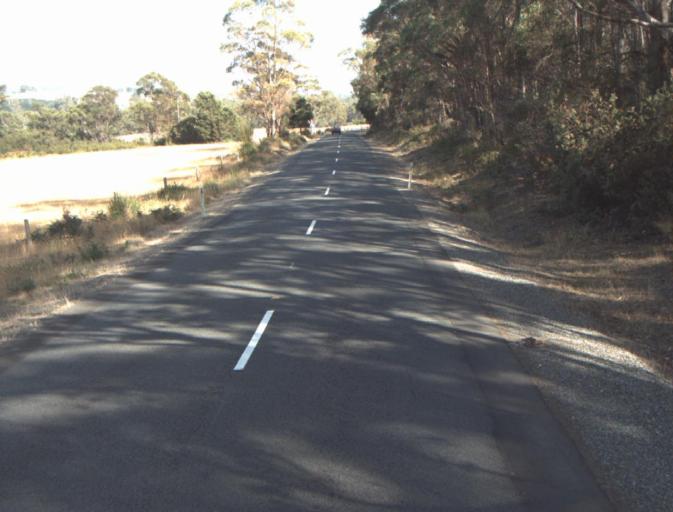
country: AU
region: Tasmania
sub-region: Dorset
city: Bridport
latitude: -41.1511
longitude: 147.2369
